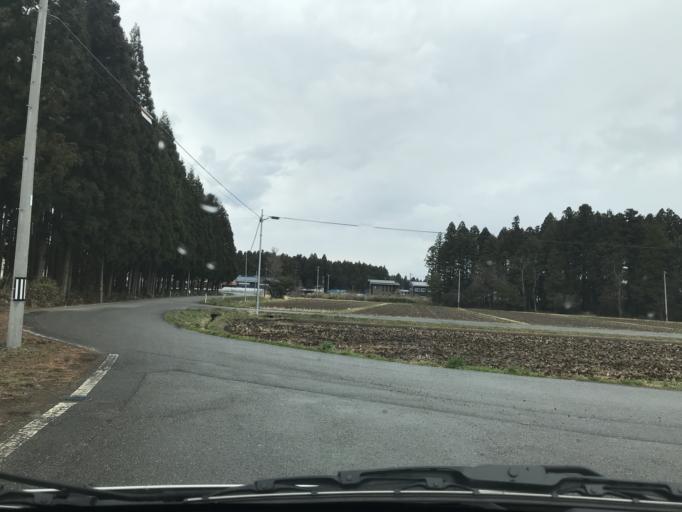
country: JP
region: Iwate
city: Mizusawa
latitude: 39.1037
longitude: 141.1070
